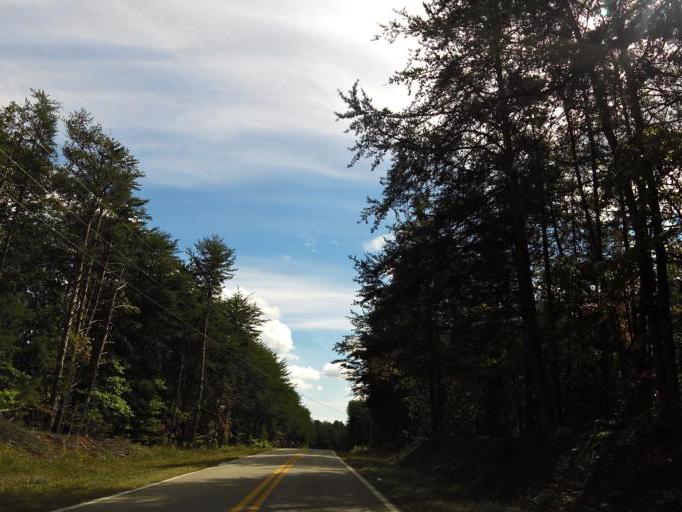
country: US
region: Georgia
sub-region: Pickens County
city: Nelson
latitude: 34.4843
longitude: -84.2589
